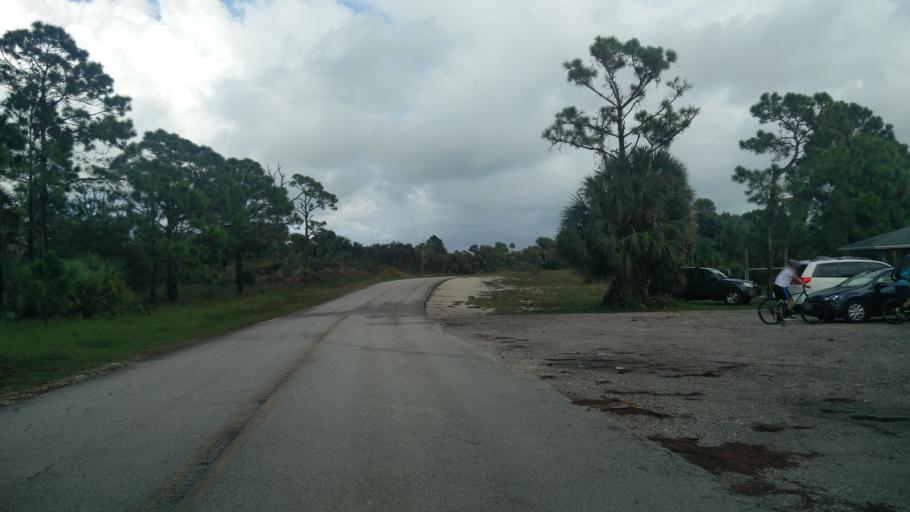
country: US
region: Florida
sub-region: Palm Beach County
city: Tequesta
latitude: 27.0119
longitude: -80.1124
